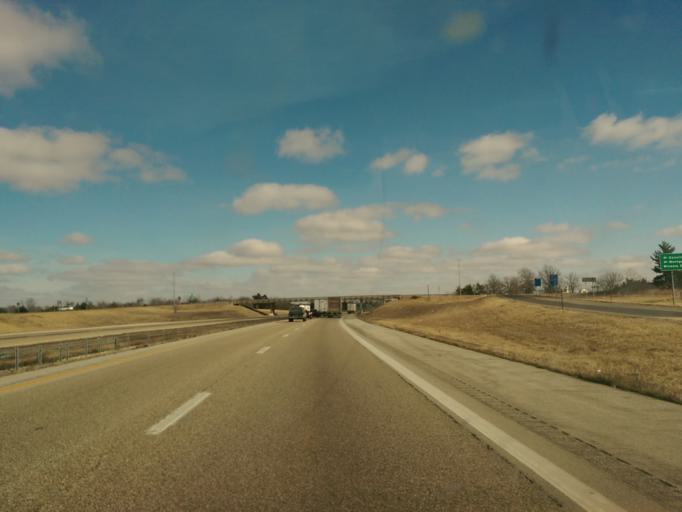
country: US
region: Missouri
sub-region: Montgomery County
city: Montgomery City
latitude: 38.9066
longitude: -91.5438
